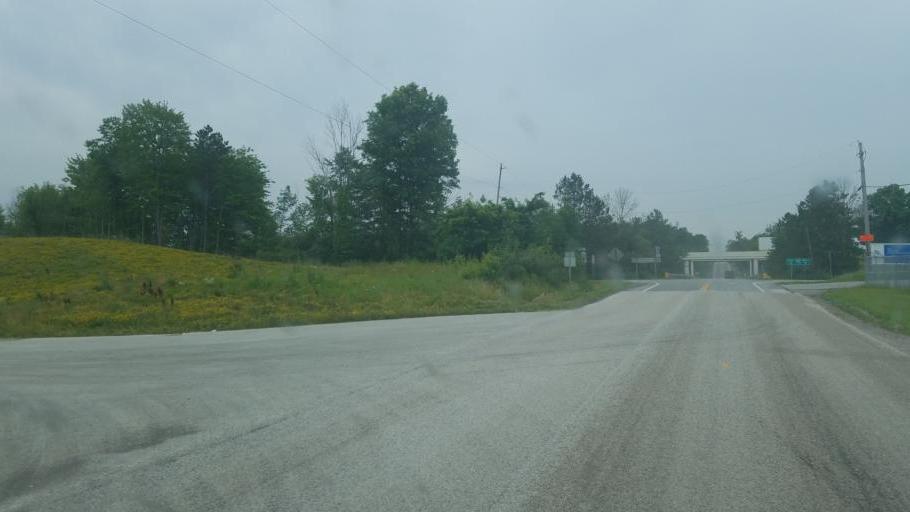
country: US
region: Ohio
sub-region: Mahoning County
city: Craig Beach
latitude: 41.1077
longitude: -81.0511
